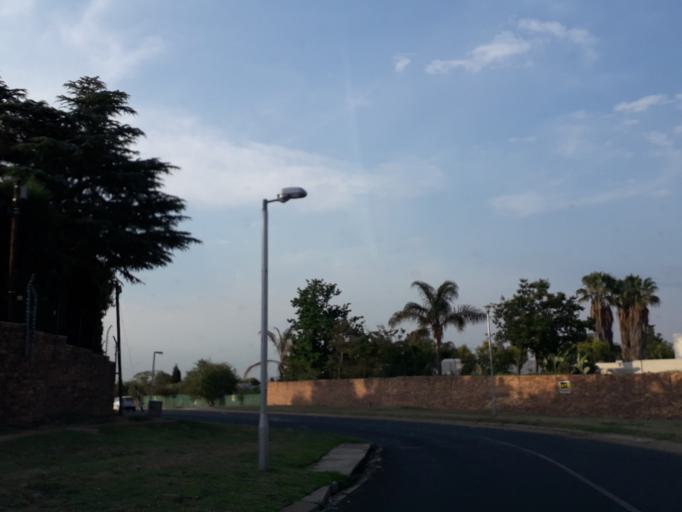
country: ZA
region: Gauteng
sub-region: City of Johannesburg Metropolitan Municipality
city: Diepsloot
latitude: -26.0029
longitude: 28.0019
